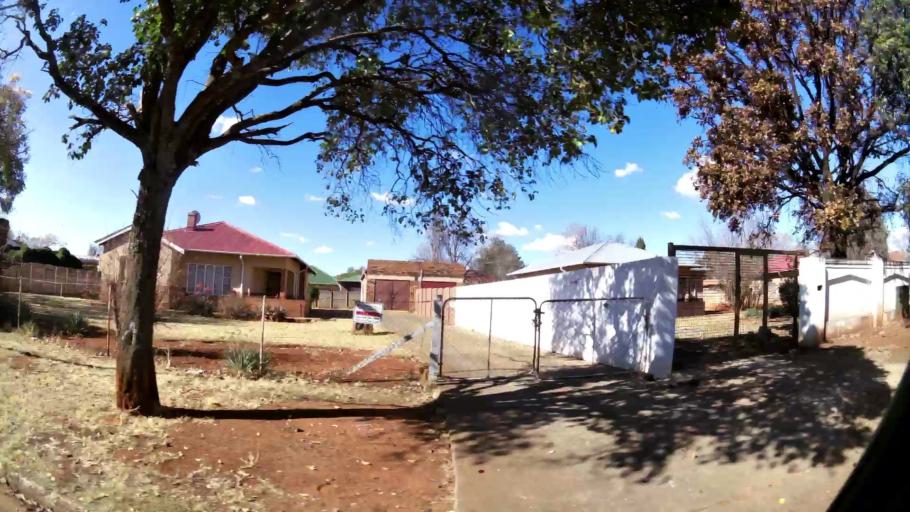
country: ZA
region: Gauteng
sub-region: West Rand District Municipality
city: Carletonville
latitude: -26.3631
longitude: 27.4012
